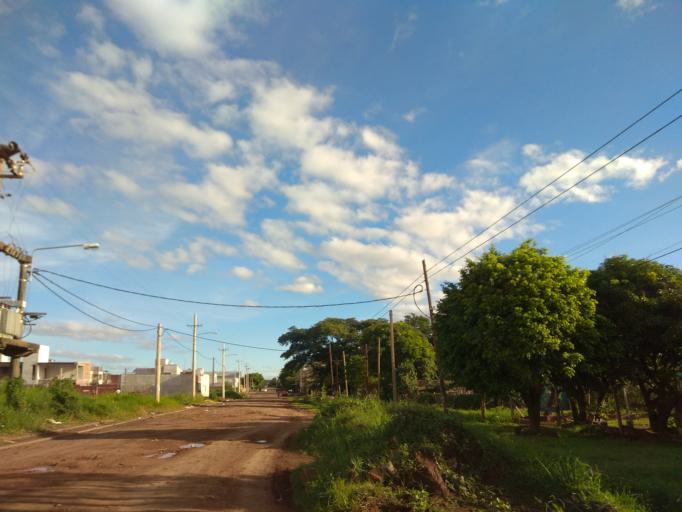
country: AR
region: Misiones
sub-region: Departamento de Capital
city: Posadas
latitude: -27.3827
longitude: -55.9262
